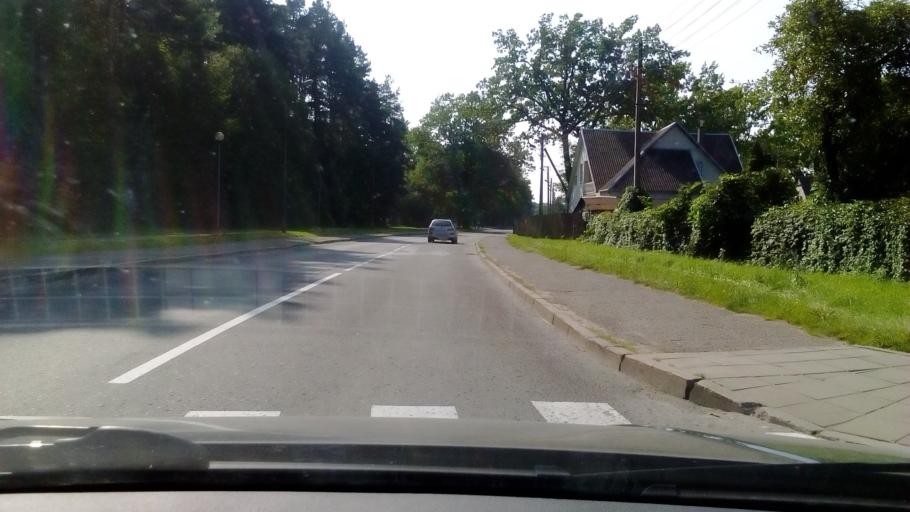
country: LT
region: Alytaus apskritis
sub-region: Alytus
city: Alytus
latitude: 54.3851
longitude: 24.0615
